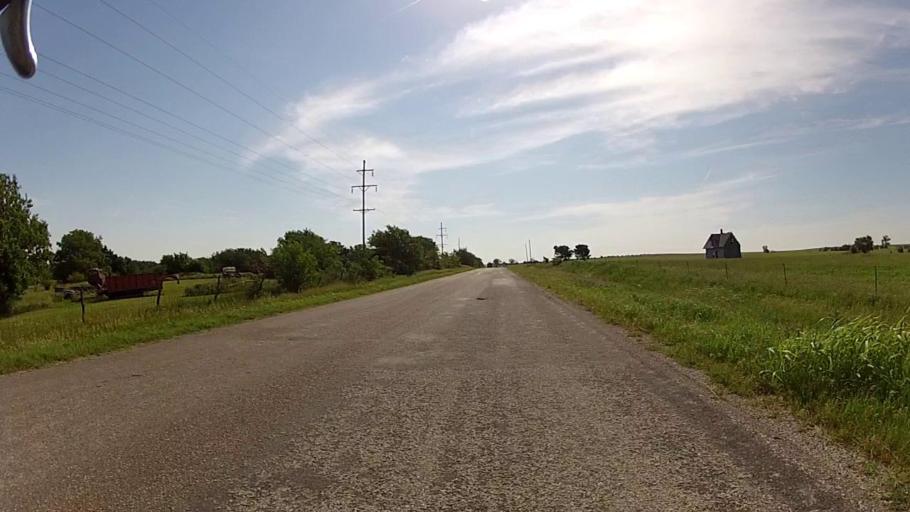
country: US
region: Kansas
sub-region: Cowley County
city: Winfield
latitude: 37.0710
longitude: -96.6631
